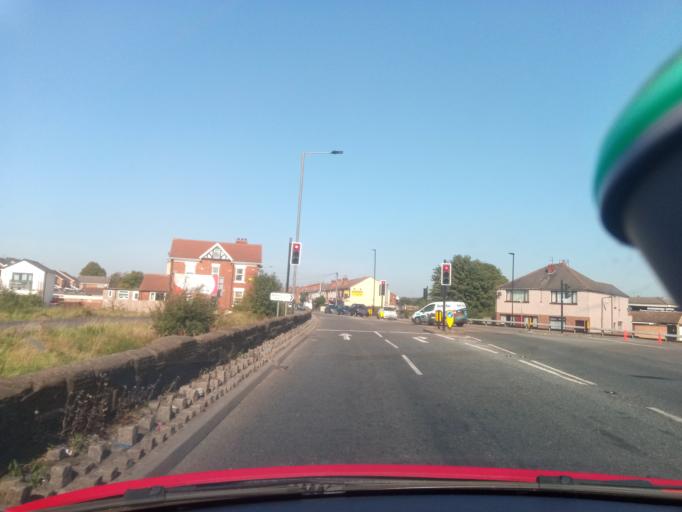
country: GB
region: England
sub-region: Doncaster
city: Bentley
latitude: 53.5357
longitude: -1.1460
